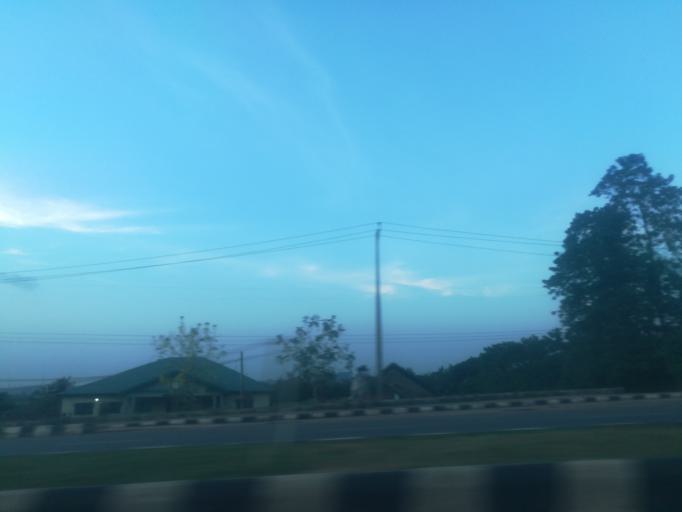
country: NG
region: Ogun
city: Abeokuta
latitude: 7.1307
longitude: 3.3627
